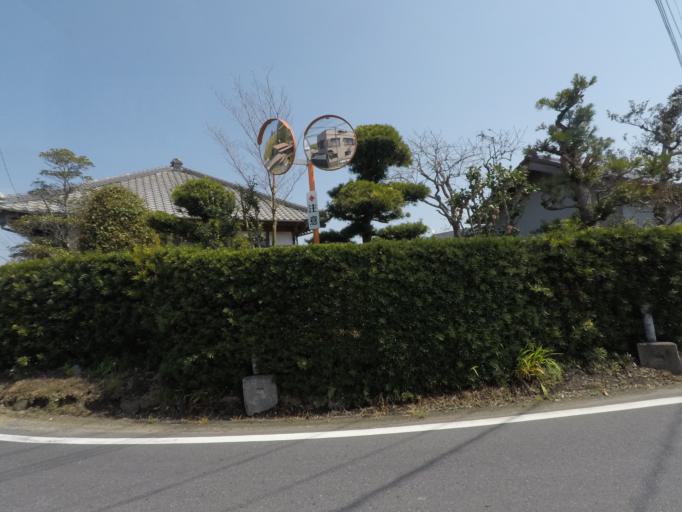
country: JP
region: Chiba
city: Yokaichiba
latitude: 35.7229
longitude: 140.4568
